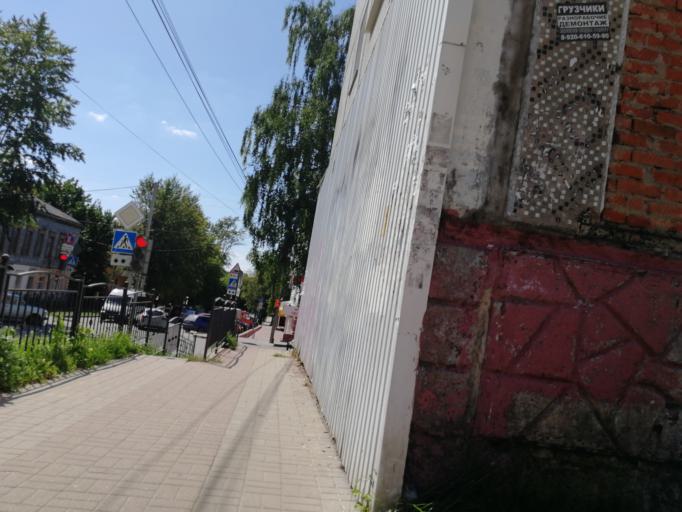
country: RU
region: Kaluga
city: Kaluga
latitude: 54.5058
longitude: 36.2734
